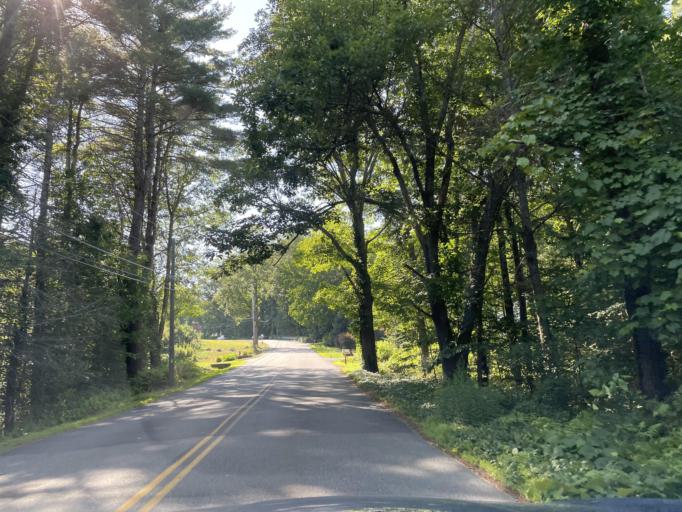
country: US
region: Massachusetts
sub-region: Worcester County
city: Charlton
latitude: 42.1612
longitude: -72.0083
